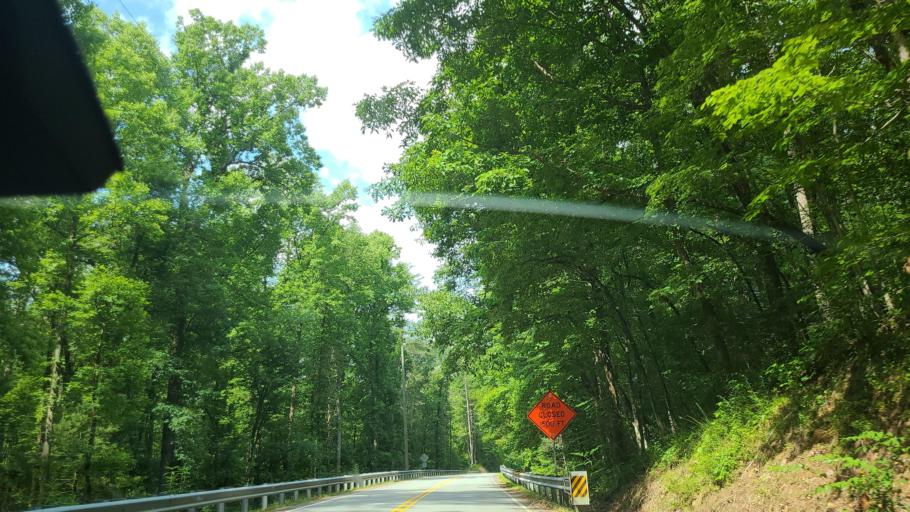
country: US
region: South Carolina
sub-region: Oconee County
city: Walhalla
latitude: 34.8675
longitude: -83.1569
